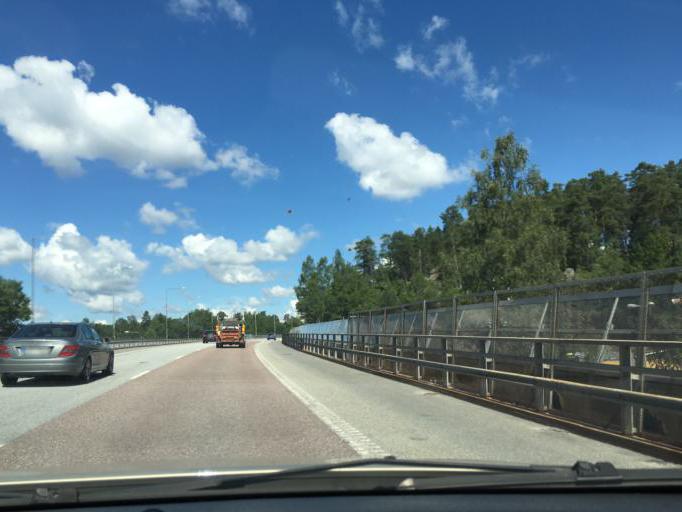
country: SE
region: Stockholm
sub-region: Nacka Kommun
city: Nacka
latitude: 59.3038
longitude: 18.1835
